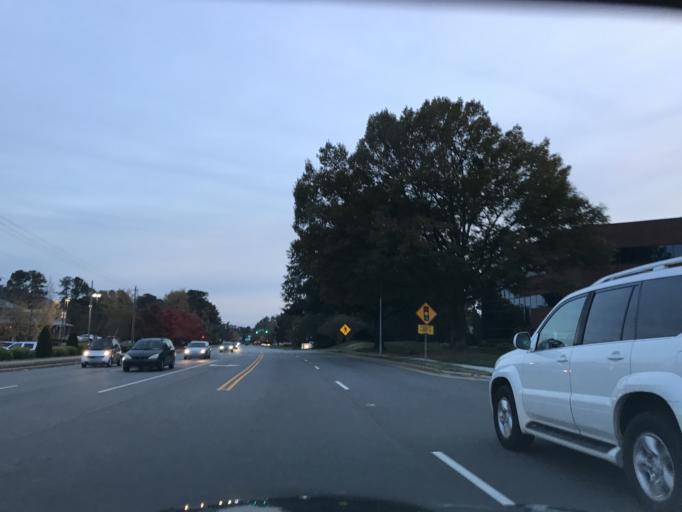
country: US
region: North Carolina
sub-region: Wake County
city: West Raleigh
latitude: 35.8659
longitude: -78.6206
